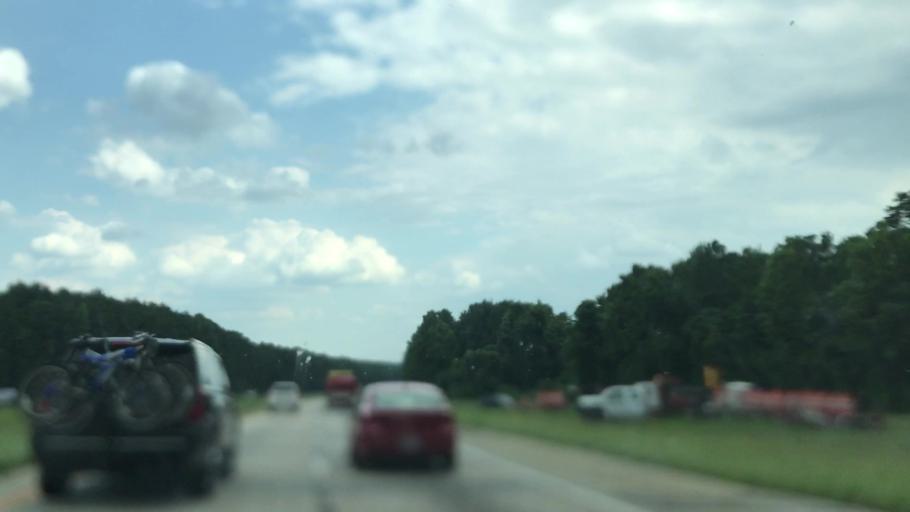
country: US
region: South Carolina
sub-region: Richland County
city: Blythewood
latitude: 34.3064
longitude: -80.9995
